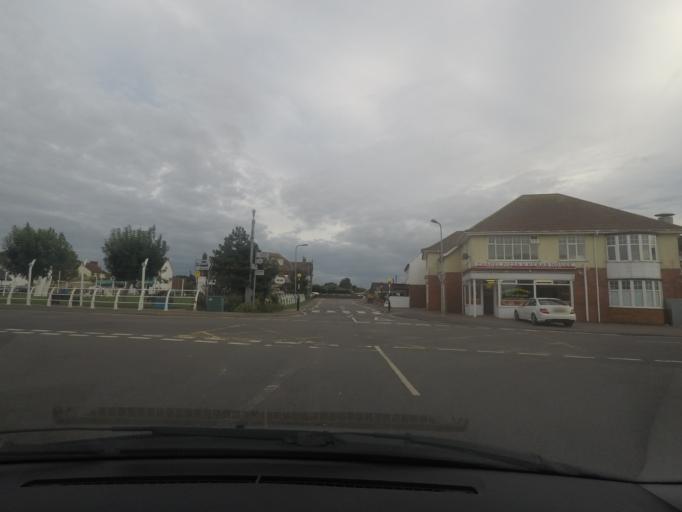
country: GB
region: England
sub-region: Lincolnshire
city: Chapel Saint Leonards
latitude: 53.2240
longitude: 0.3366
